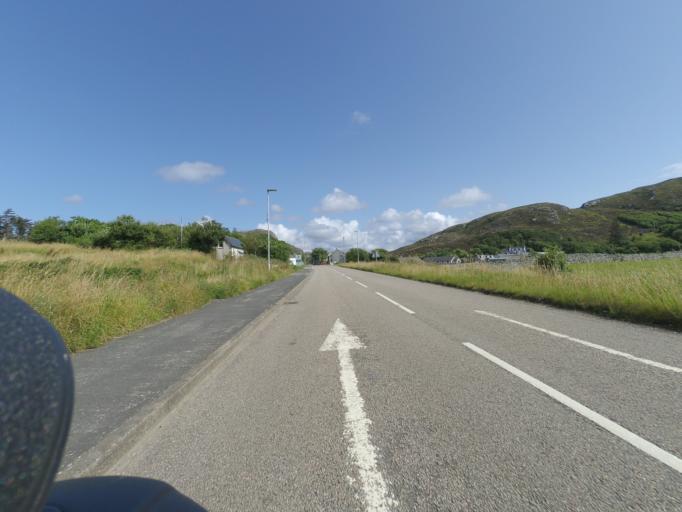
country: GB
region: Scotland
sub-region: Highland
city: Ullapool
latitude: 58.3515
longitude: -5.1541
